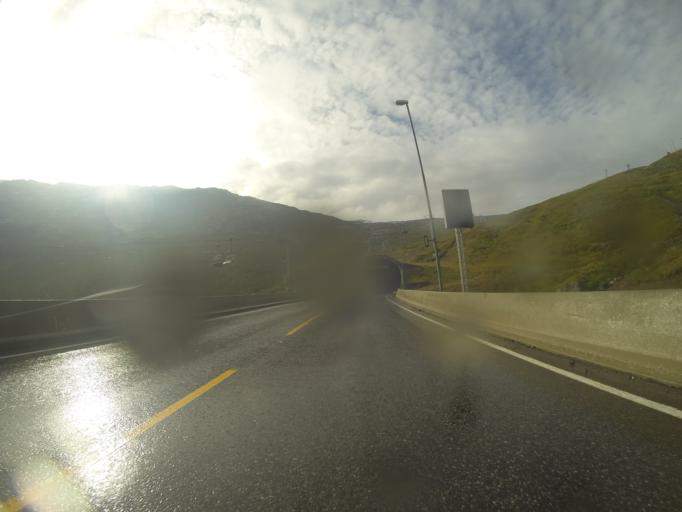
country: NO
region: Hordaland
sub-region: Odda
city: Odda
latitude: 59.8229
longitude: 6.7387
